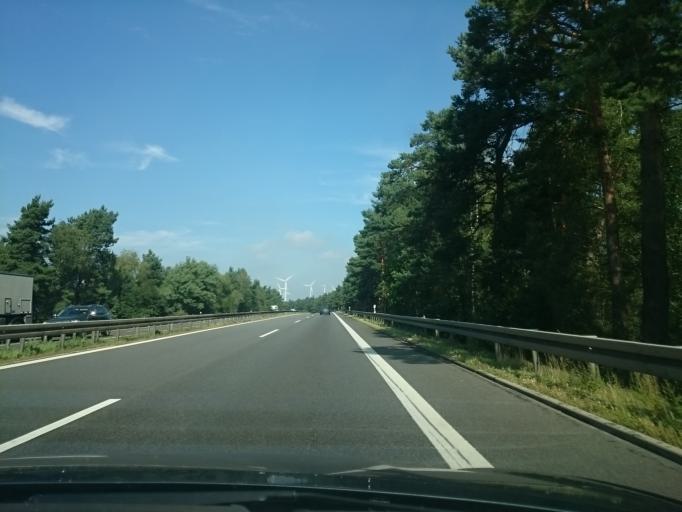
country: DE
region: Brandenburg
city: Bronkow
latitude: 51.7081
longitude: 13.8964
